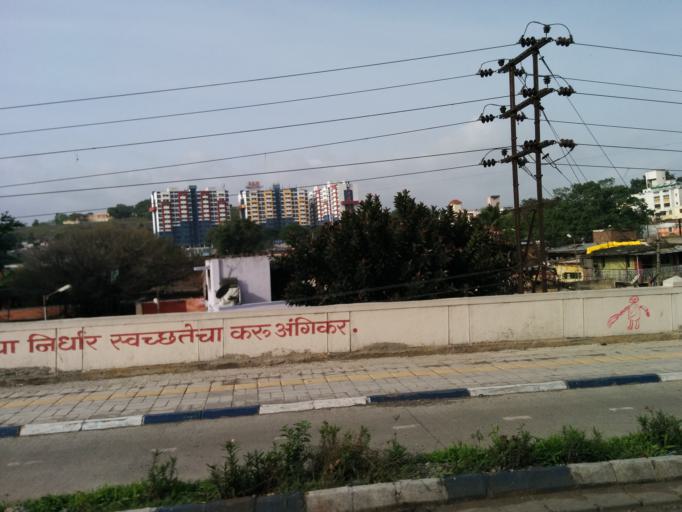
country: IN
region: Maharashtra
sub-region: Pune Division
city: Pune
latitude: 18.5059
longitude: 73.9148
